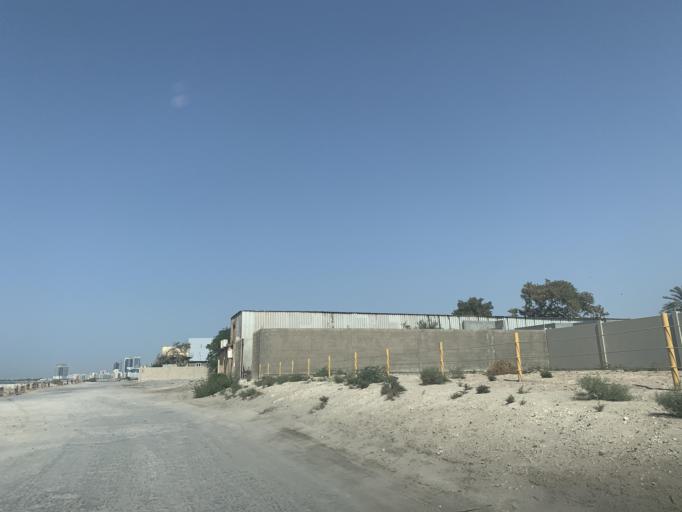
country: BH
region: Manama
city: Jidd Hafs
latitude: 26.2356
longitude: 50.5038
